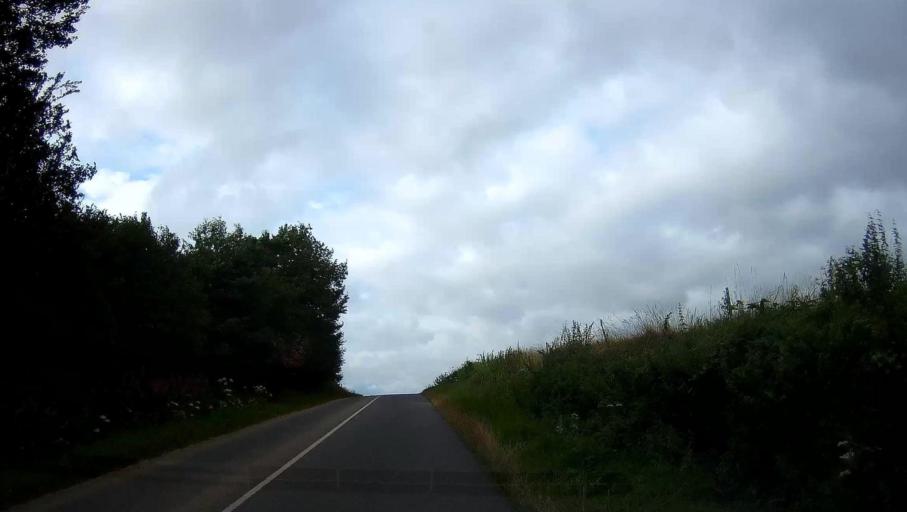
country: FR
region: Champagne-Ardenne
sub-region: Departement des Ardennes
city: Chateau-Porcien
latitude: 49.6231
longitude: 4.2348
